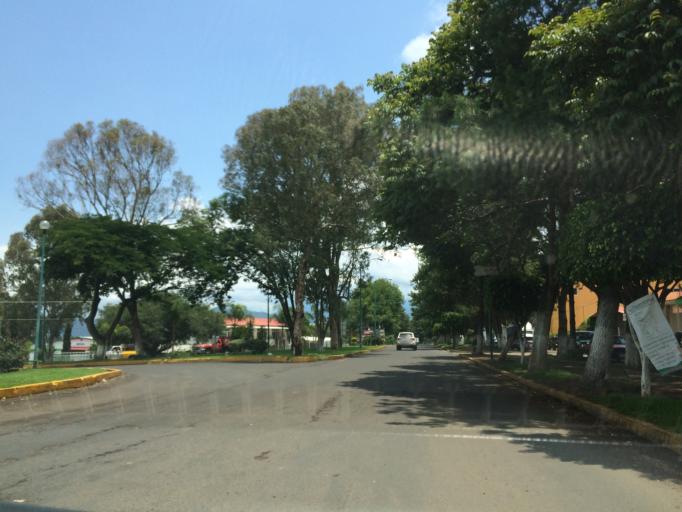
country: MX
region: Michoacan
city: Periban de Ramos
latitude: 19.5301
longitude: -102.4123
